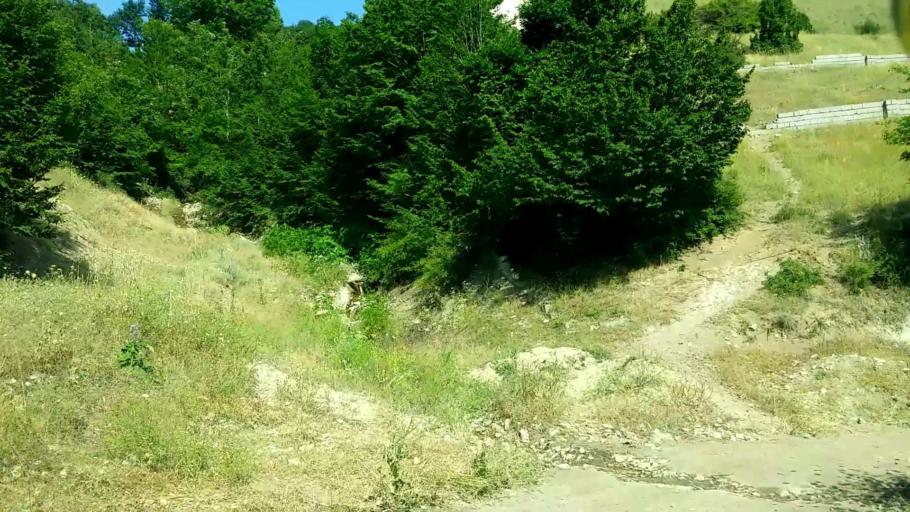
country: IR
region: Mazandaran
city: Chalus
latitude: 36.5540
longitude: 51.2950
